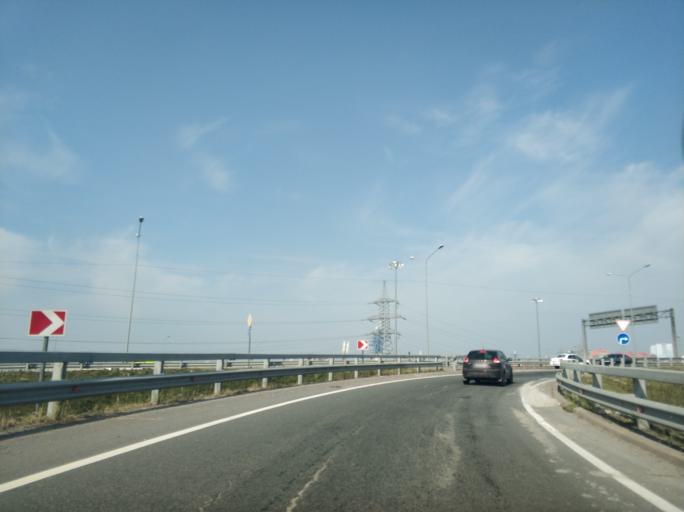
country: RU
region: Leningrad
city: Murino
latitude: 60.0159
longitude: 30.4601
